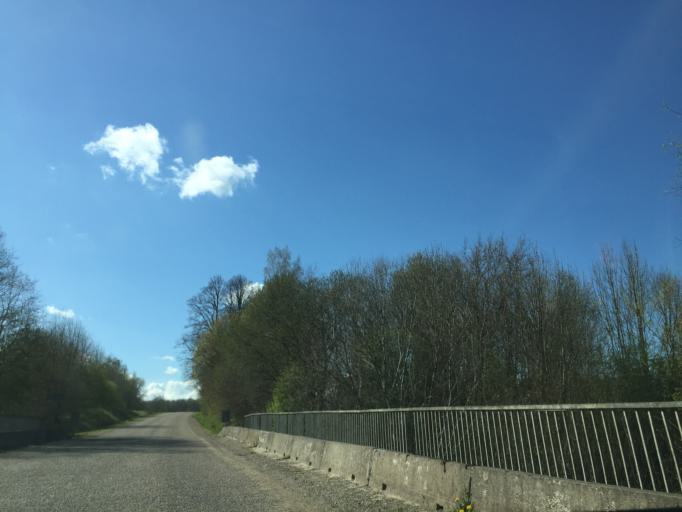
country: LV
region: Strenci
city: Strenci
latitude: 57.5059
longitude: 25.6742
